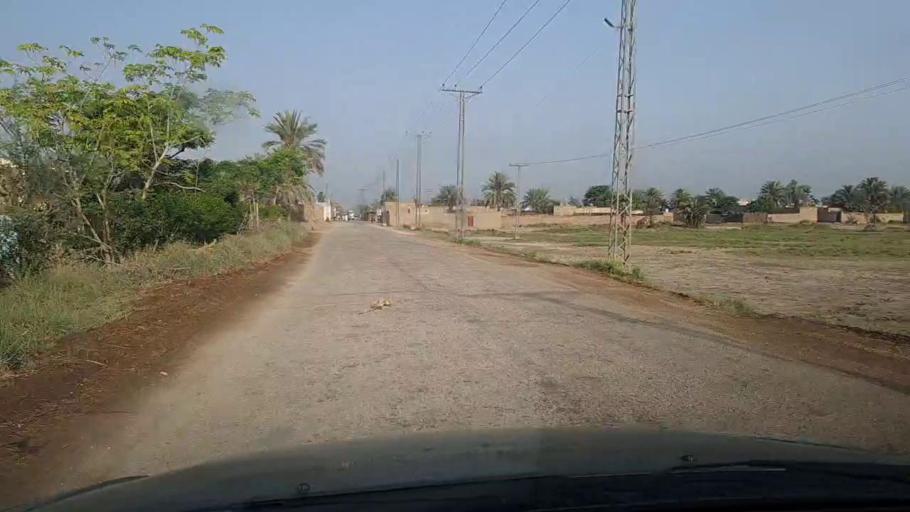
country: PK
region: Sindh
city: Pir jo Goth
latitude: 27.5701
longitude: 68.6301
